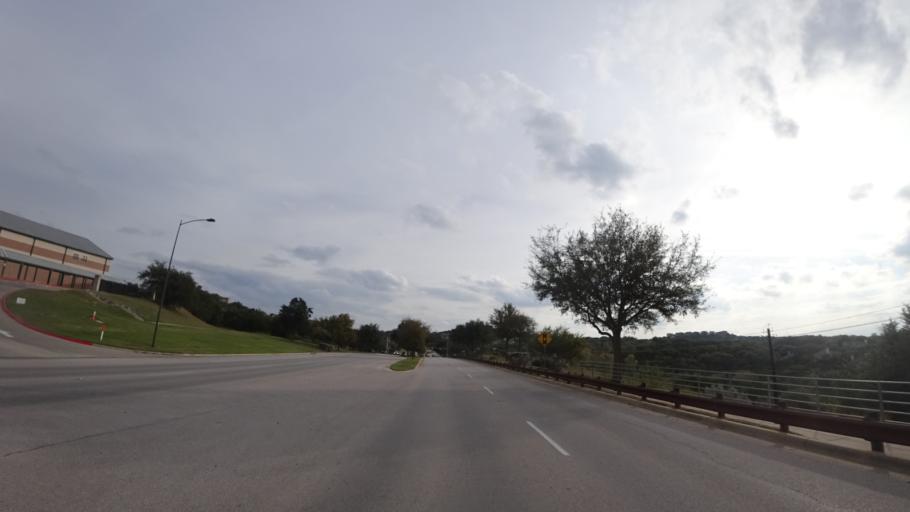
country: US
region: Texas
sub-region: Travis County
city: Hudson Bend
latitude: 30.3794
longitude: -97.8852
